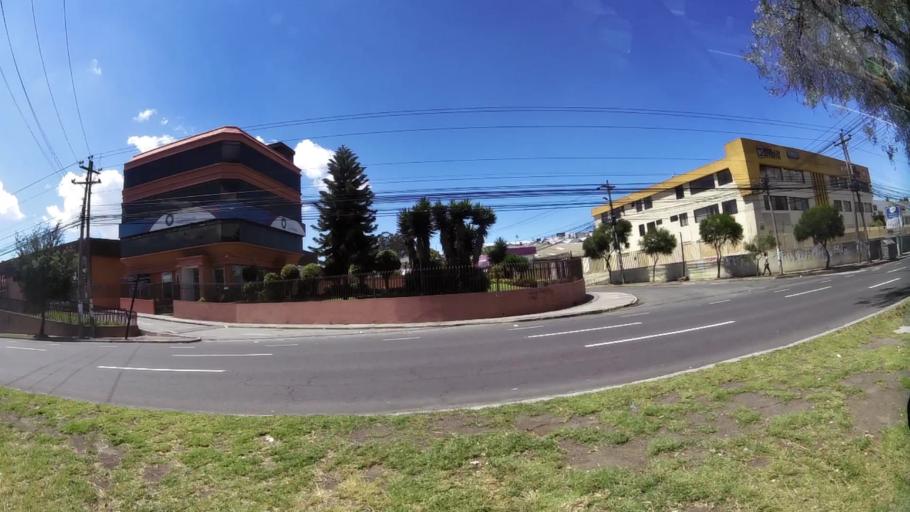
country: EC
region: Pichincha
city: Quito
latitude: -0.1104
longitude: -78.4787
